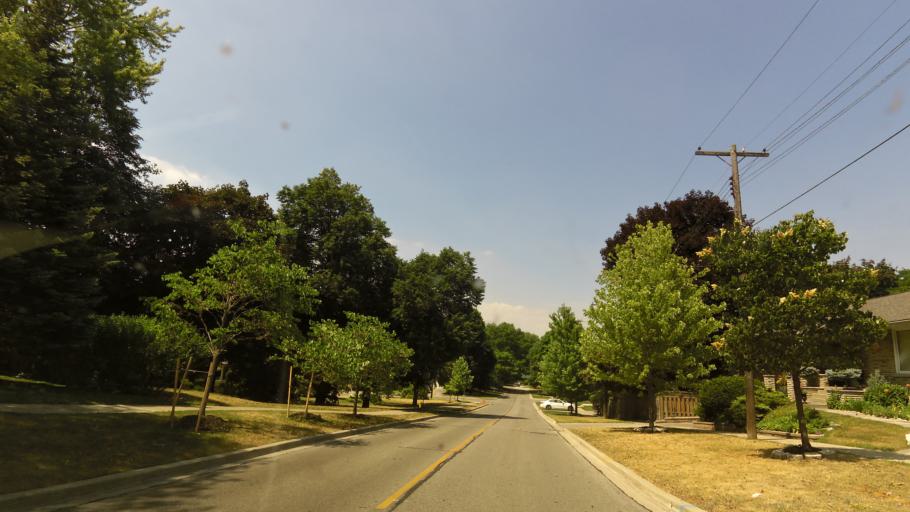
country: CA
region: Ontario
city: Etobicoke
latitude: 43.6400
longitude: -79.4950
